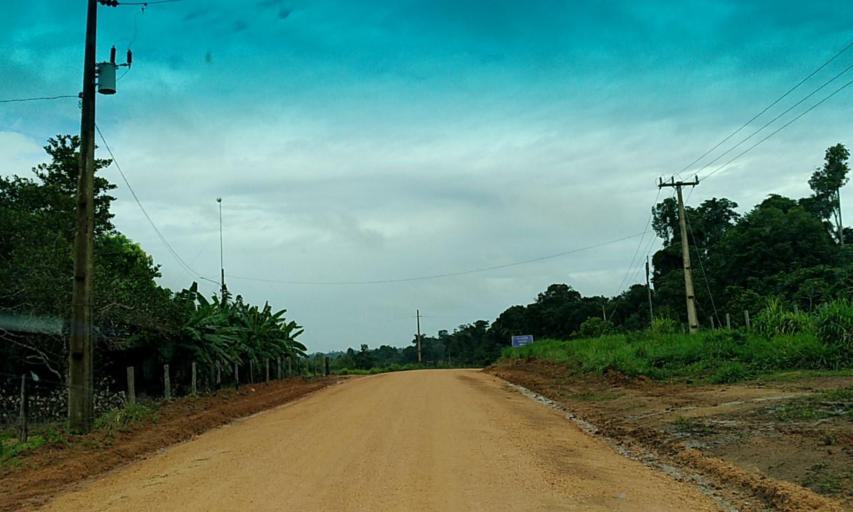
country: BR
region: Para
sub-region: Senador Jose Porfirio
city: Senador Jose Porfirio
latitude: -3.0214
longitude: -51.6811
